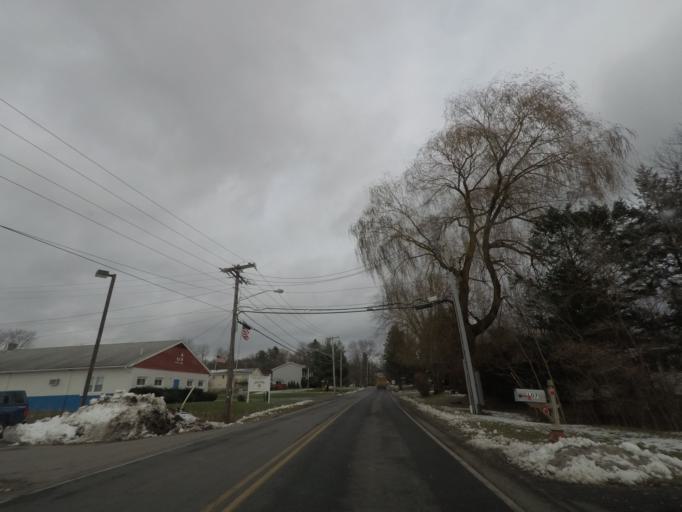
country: US
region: New York
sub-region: Rensselaer County
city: East Greenbush
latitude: 42.5871
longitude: -73.7082
